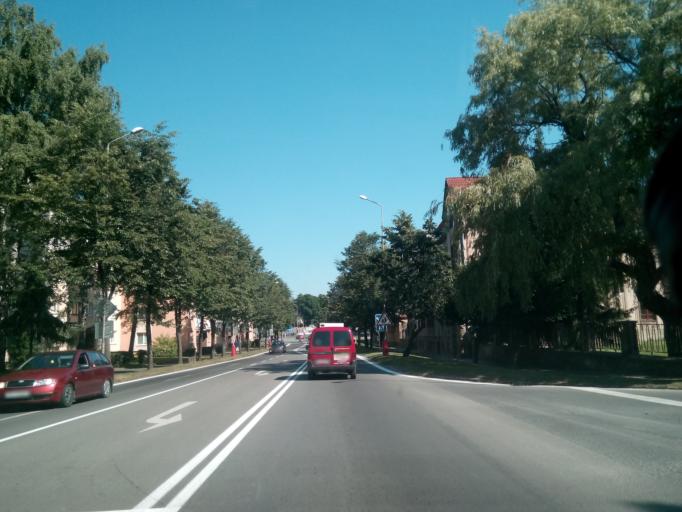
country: SK
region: Presovsky
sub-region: Okres Presov
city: Kezmarok
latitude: 49.1365
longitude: 20.4266
